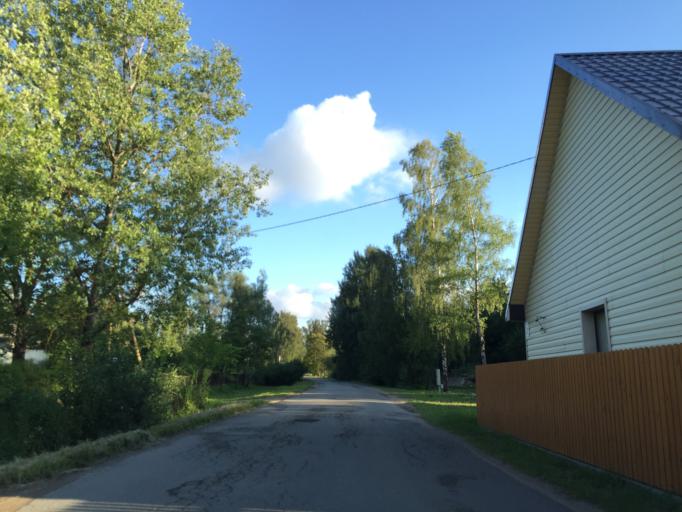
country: LV
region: Sigulda
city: Sigulda
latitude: 57.1427
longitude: 24.8311
